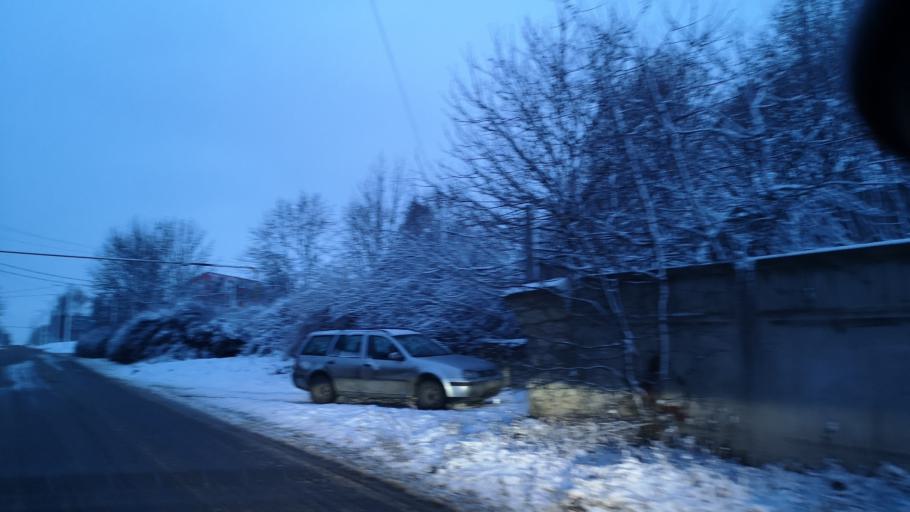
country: MD
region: Rezina
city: Rezina
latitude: 47.7547
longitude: 28.9559
